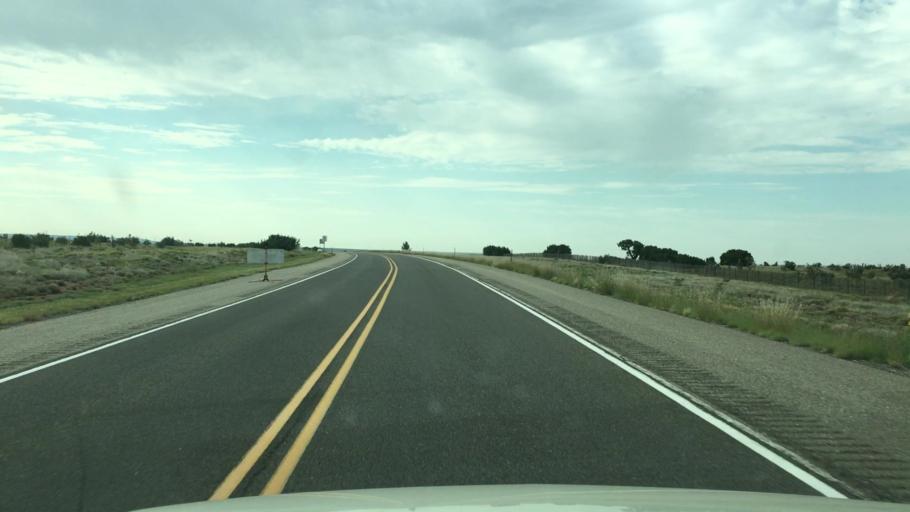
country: US
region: New Mexico
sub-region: Santa Fe County
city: Eldorado at Santa Fe
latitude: 35.2217
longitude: -105.8009
